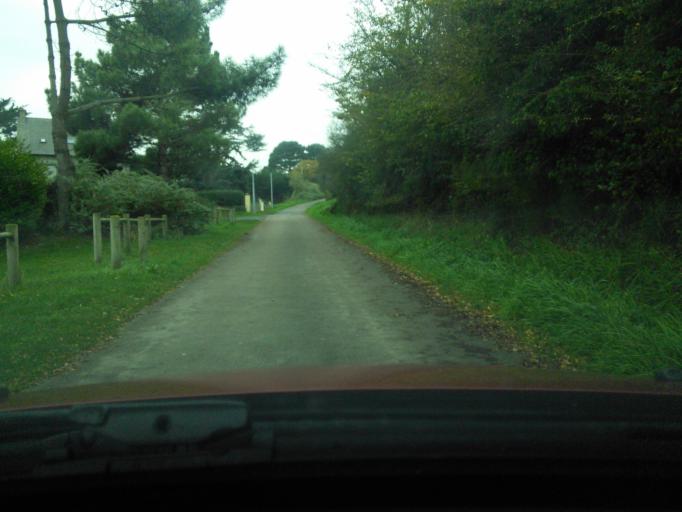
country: FR
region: Brittany
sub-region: Departement des Cotes-d'Armor
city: Hillion
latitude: 48.5309
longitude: -2.6641
